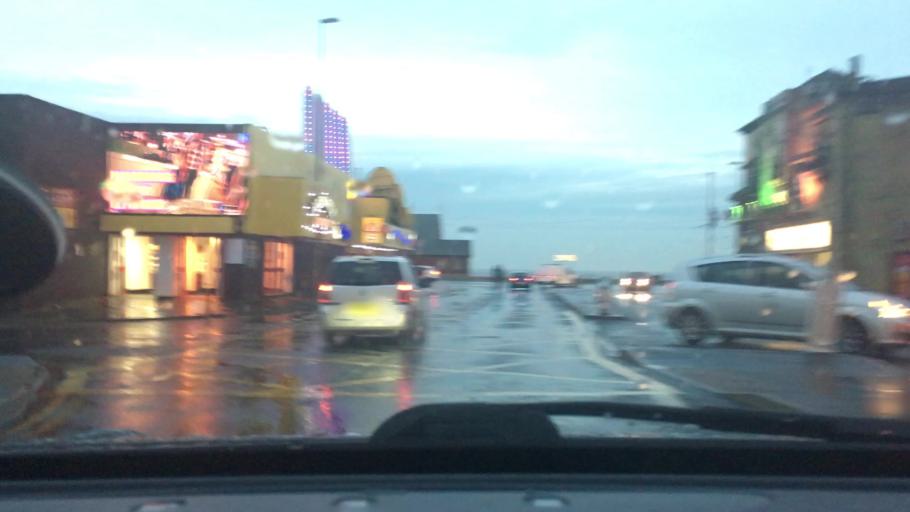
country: GB
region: England
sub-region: Blackpool
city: Blackpool
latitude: 53.8137
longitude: -3.0543
